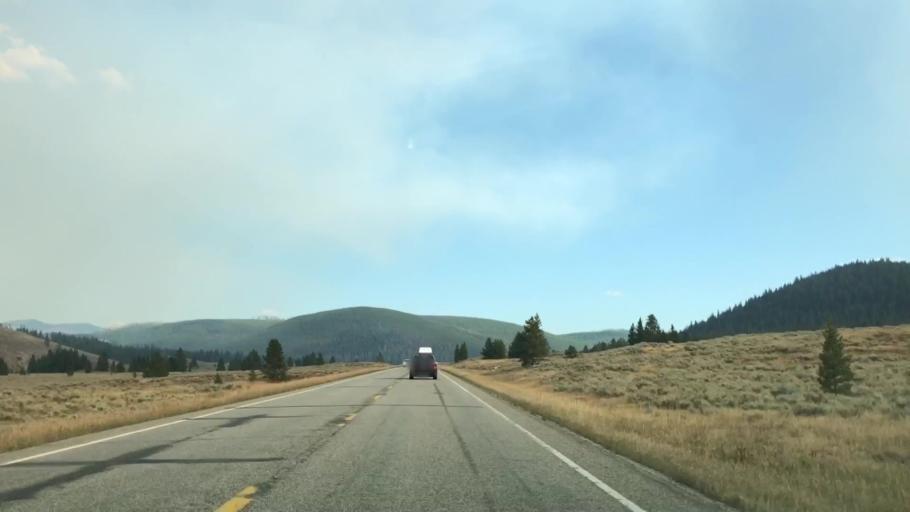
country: US
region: Montana
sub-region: Gallatin County
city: West Yellowstone
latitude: 44.9593
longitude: -111.0702
